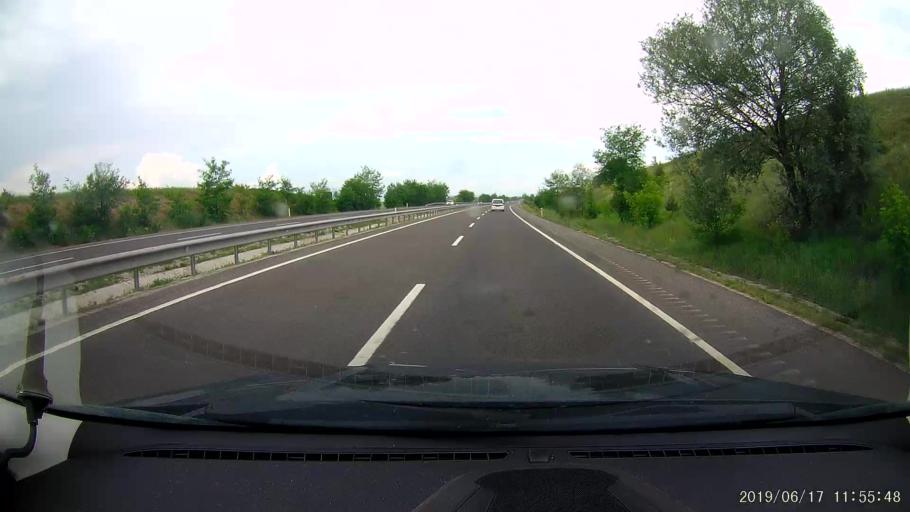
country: TR
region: Cankiri
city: Atkaracalar
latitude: 40.8007
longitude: 32.9982
